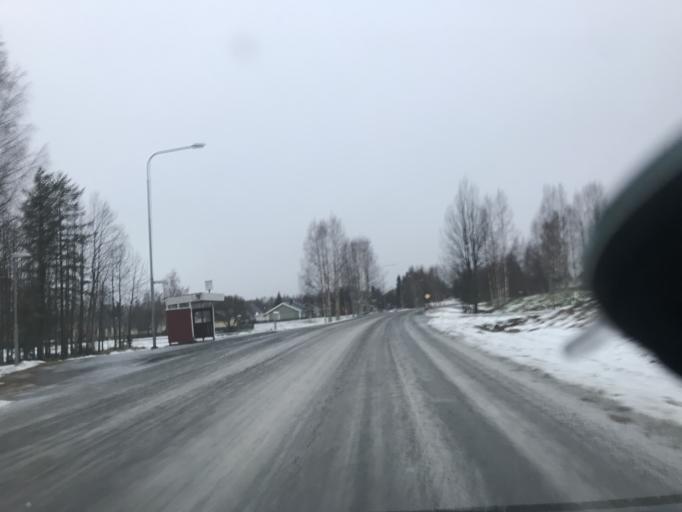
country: SE
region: Norrbotten
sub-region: Lulea Kommun
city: Sodra Sunderbyn
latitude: 65.6529
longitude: 21.9499
